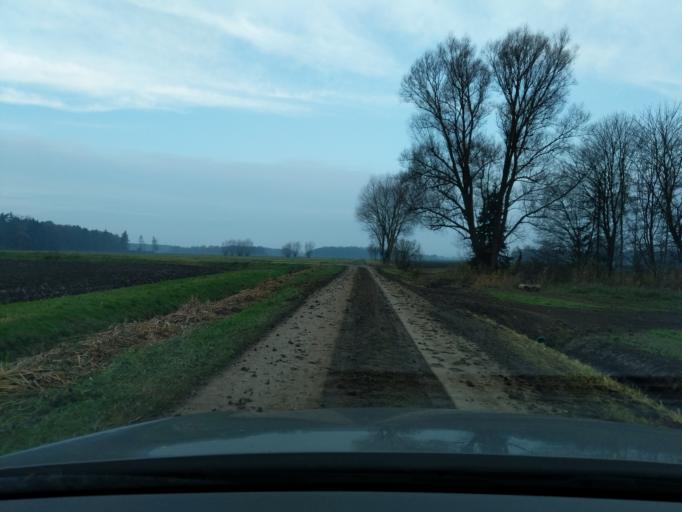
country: DE
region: Lower Saxony
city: Brietlingen
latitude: 53.3653
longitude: 10.4550
